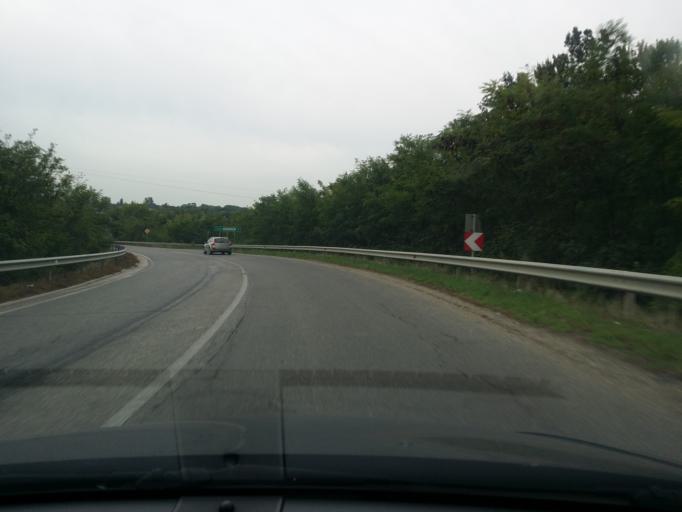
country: HU
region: Pest
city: Gyal
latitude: 47.3535
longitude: 19.1947
